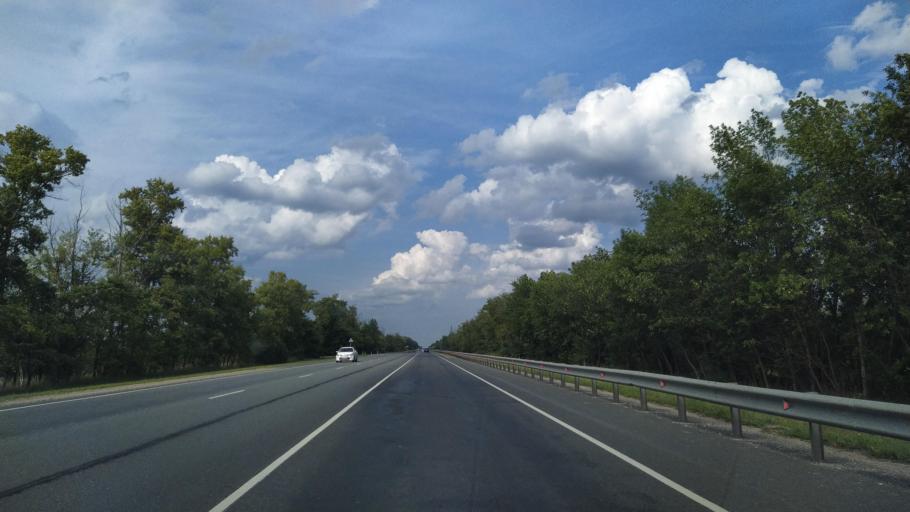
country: RU
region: Novgorod
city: Shimsk
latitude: 58.2241
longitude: 30.7453
